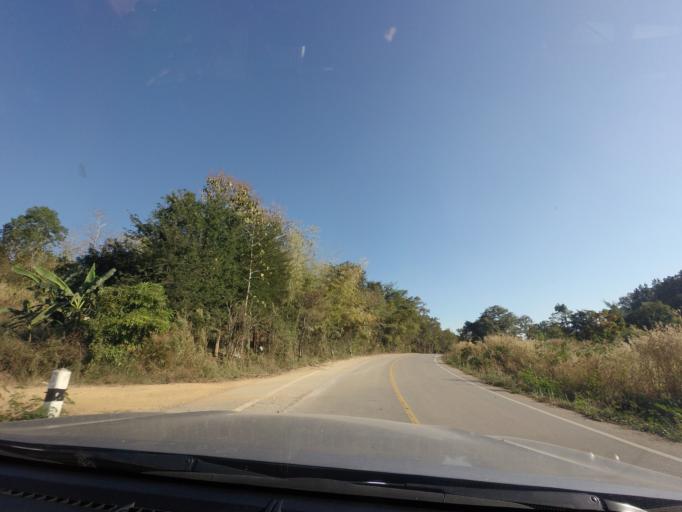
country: TH
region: Lampang
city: Chae Hom
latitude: 18.5400
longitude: 99.6409
